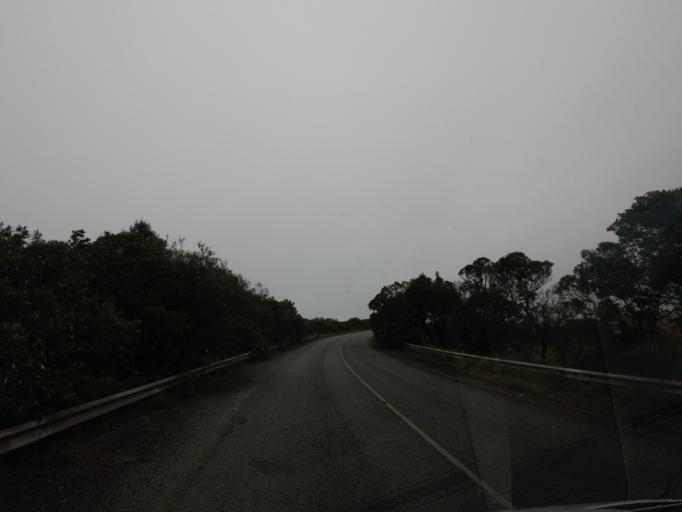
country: ZA
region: Mpumalanga
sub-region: Ehlanzeni District
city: Graksop
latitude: -24.8659
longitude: 30.8972
